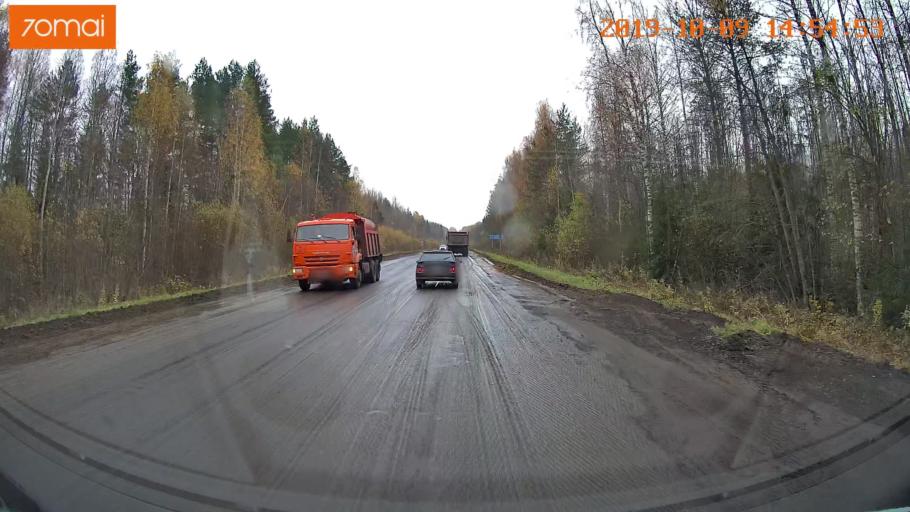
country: RU
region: Kostroma
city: Chistyye Bory
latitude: 58.3539
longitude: 41.6440
